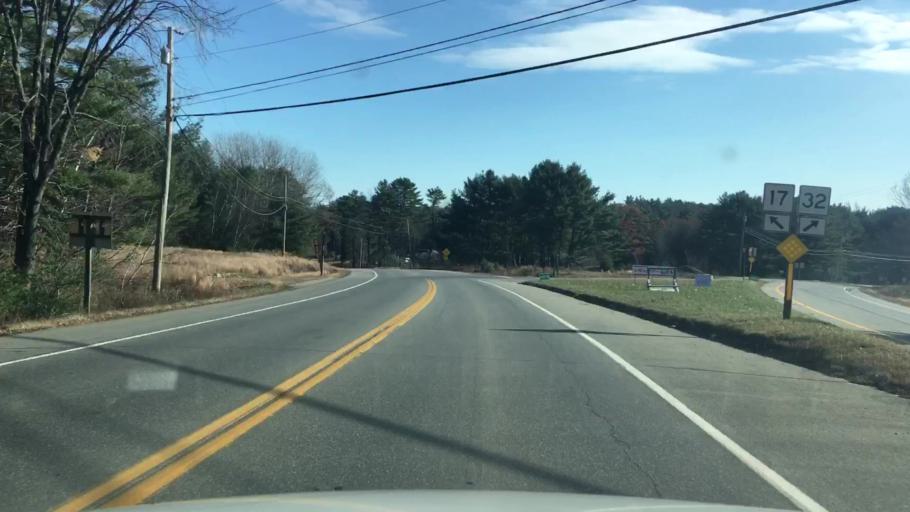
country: US
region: Maine
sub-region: Kennebec County
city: Windsor
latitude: 44.2511
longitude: -69.5398
